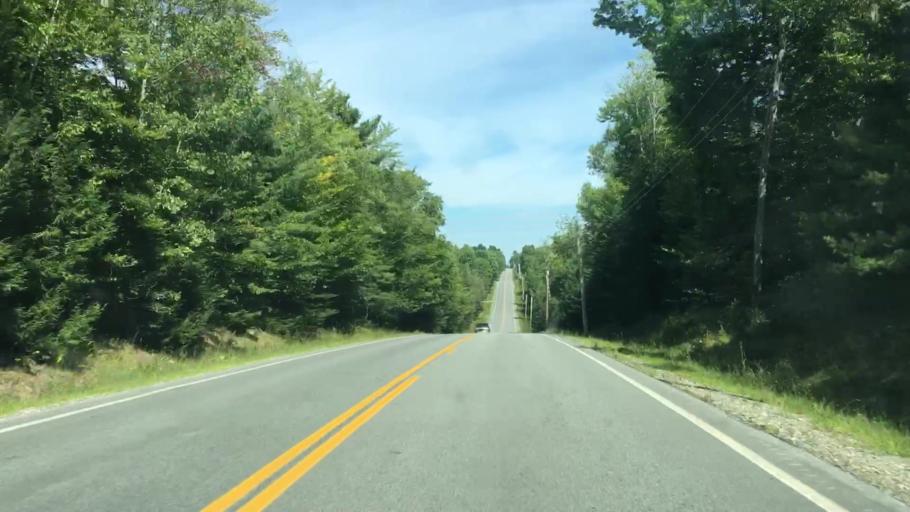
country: US
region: Maine
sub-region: Penobscot County
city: Howland
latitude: 45.2086
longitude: -68.8034
